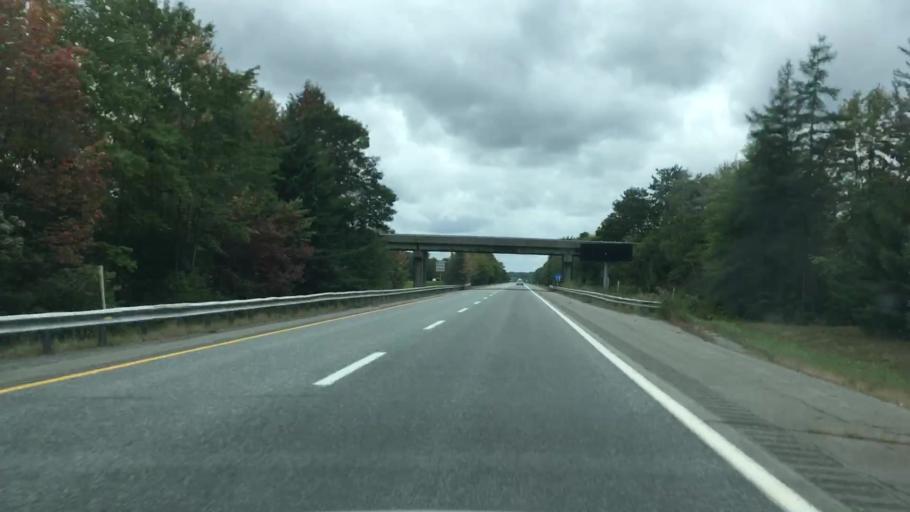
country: US
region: Maine
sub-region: Penobscot County
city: Veazie
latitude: 44.8470
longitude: -68.7302
